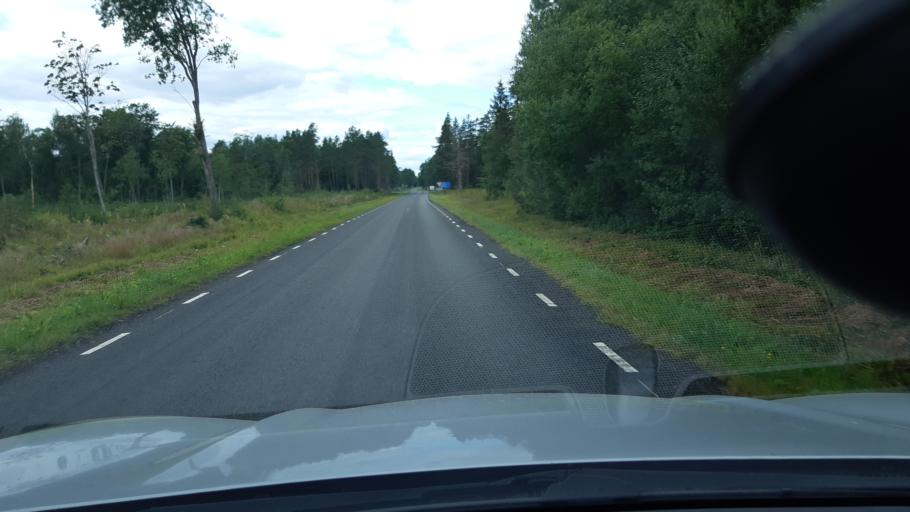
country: EE
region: Raplamaa
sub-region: Rapla vald
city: Rapla
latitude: 58.8850
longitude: 24.7287
